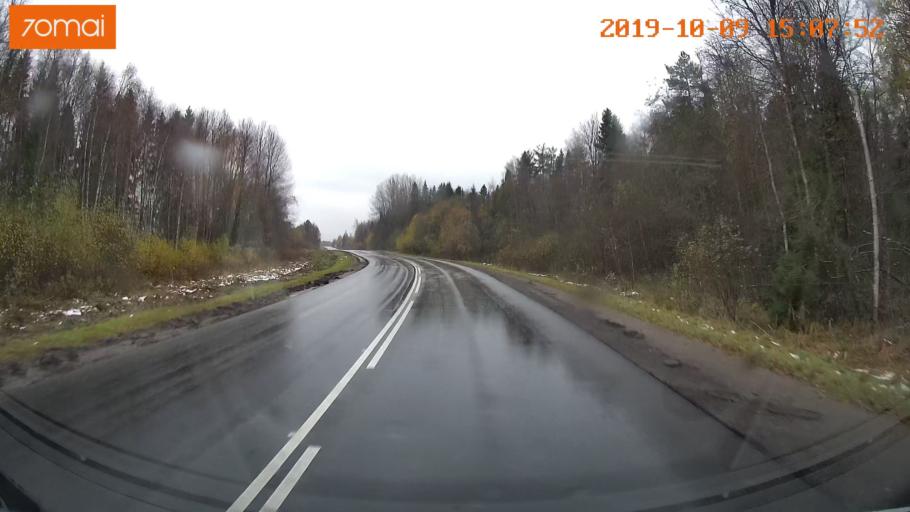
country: RU
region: Kostroma
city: Susanino
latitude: 58.2139
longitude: 41.6465
